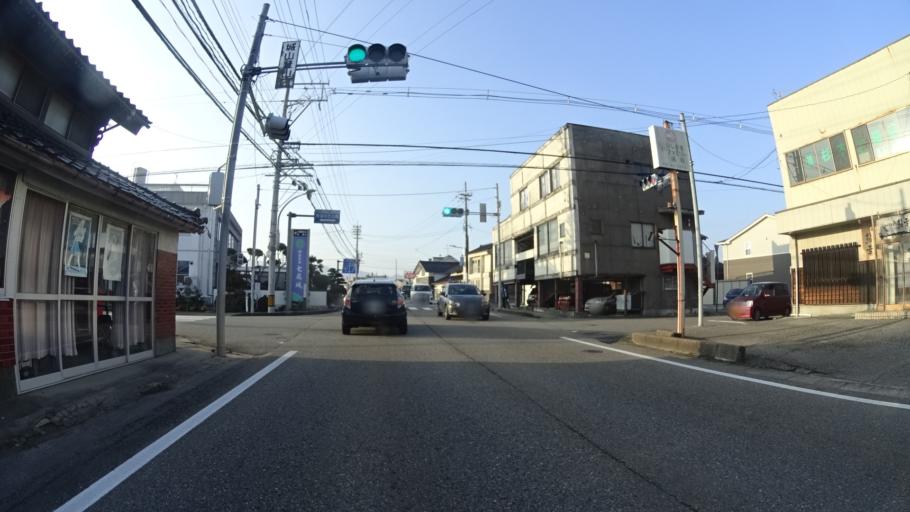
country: JP
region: Ishikawa
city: Nanao
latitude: 37.0333
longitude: 136.9679
